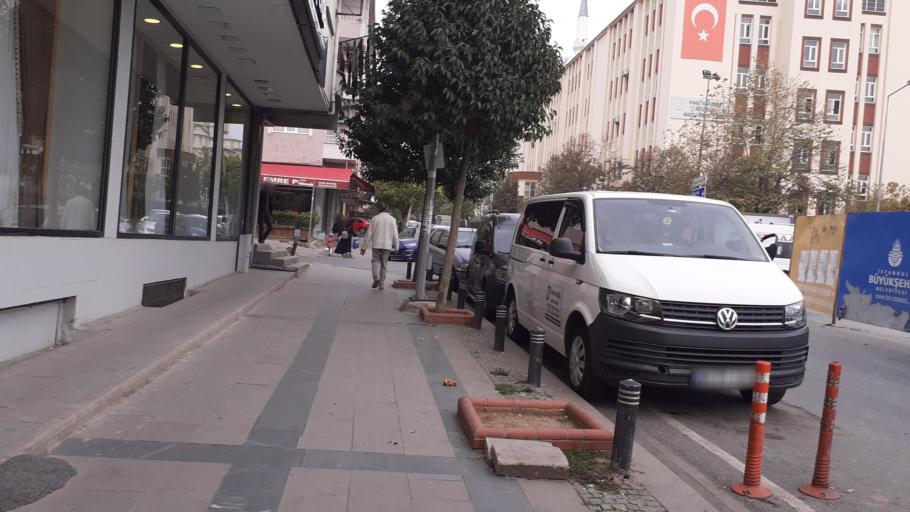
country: TR
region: Istanbul
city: Mahmutbey
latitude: 40.9904
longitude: 28.7825
